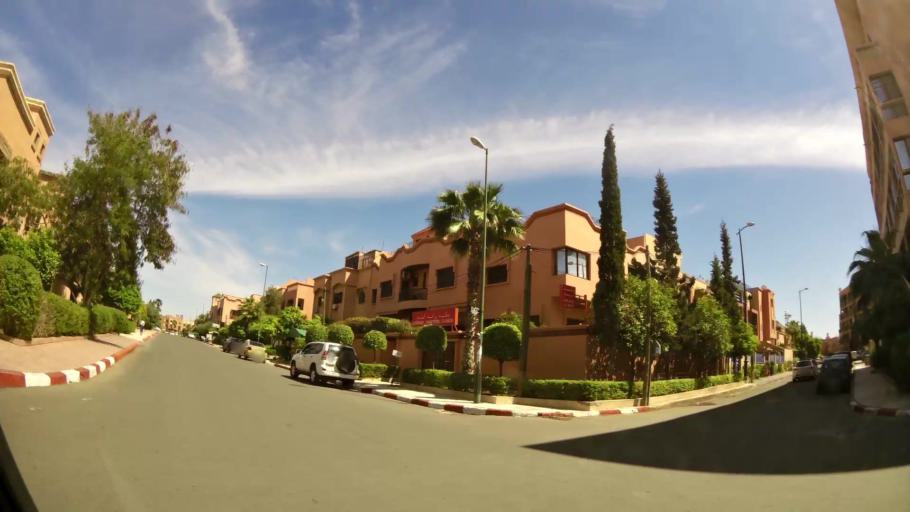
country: MA
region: Marrakech-Tensift-Al Haouz
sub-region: Marrakech
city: Marrakesh
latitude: 31.6622
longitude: -8.0038
